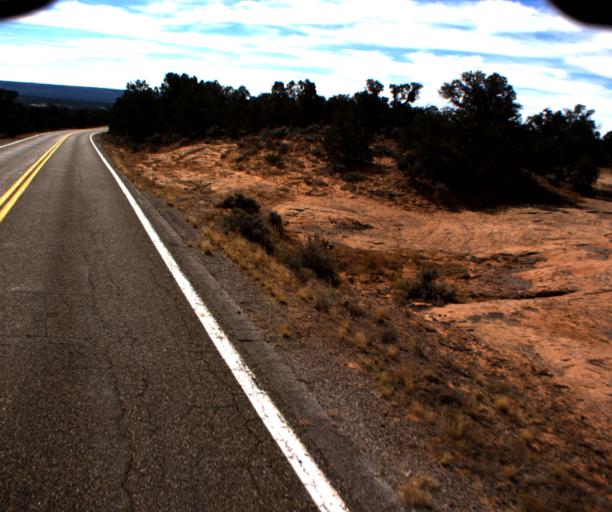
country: US
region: Arizona
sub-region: Navajo County
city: Kayenta
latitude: 36.6325
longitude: -110.5094
